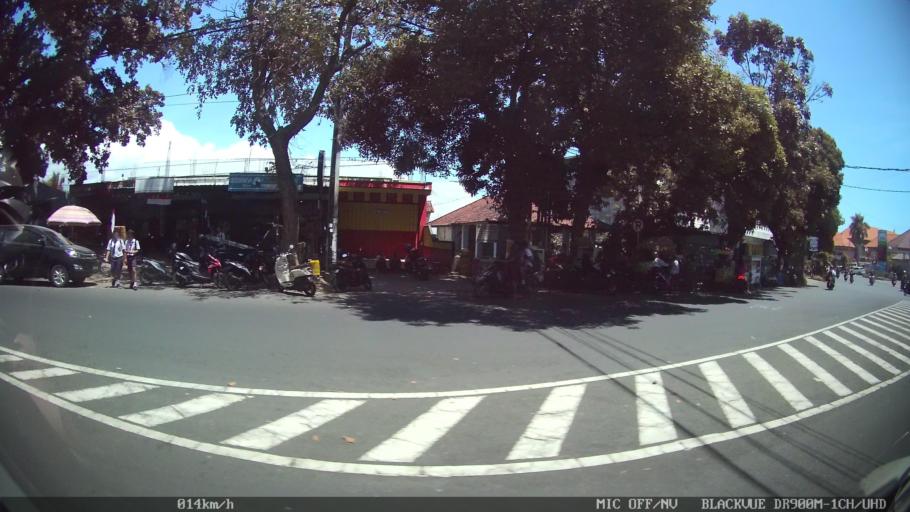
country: ID
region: Bali
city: Banjar Kaliuntu Satu
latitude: -8.1155
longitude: 115.0803
